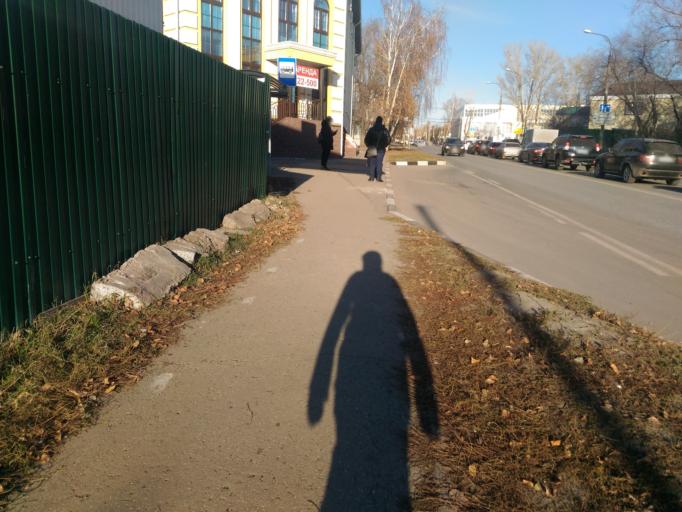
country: RU
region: Ulyanovsk
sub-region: Ulyanovskiy Rayon
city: Ulyanovsk
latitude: 54.3143
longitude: 48.3800
